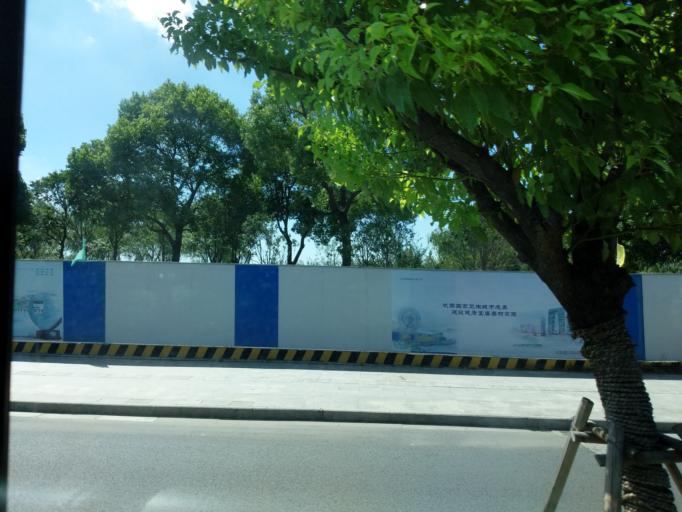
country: CN
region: Jiangsu Sheng
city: Weiting
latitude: 31.3255
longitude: 120.6793
